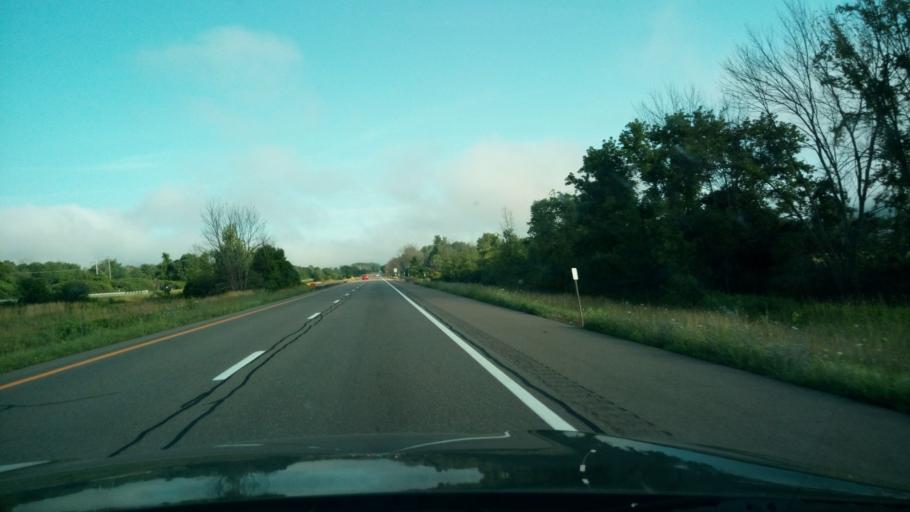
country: US
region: New York
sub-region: Steuben County
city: Bath
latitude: 42.2631
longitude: -77.2147
